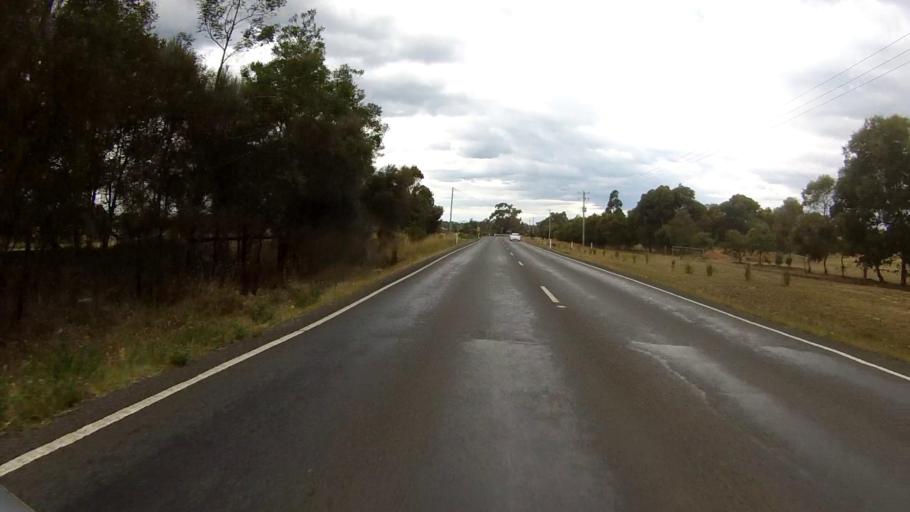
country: AU
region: Tasmania
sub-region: Clarence
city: Cambridge
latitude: -42.8443
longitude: 147.4757
